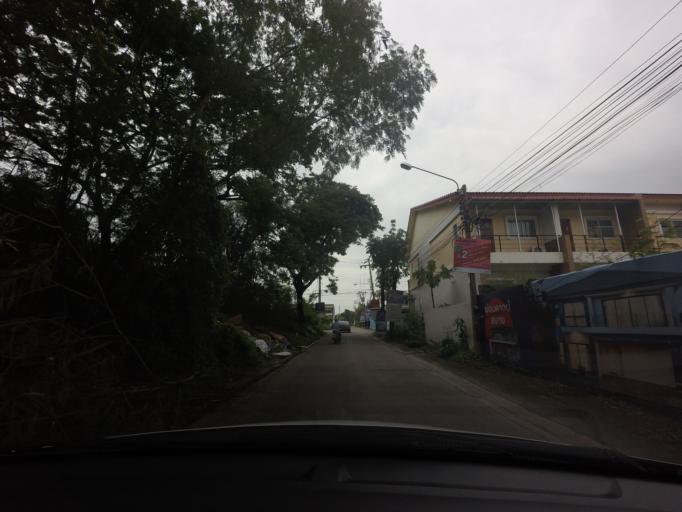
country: TH
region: Bangkok
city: Lak Si
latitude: 13.8974
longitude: 100.5719
